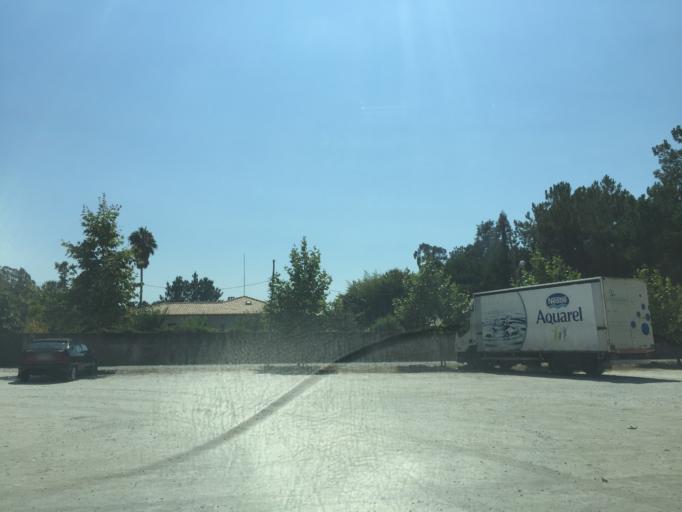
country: PT
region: Coimbra
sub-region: Mira
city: Mira
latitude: 40.3418
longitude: -8.7277
